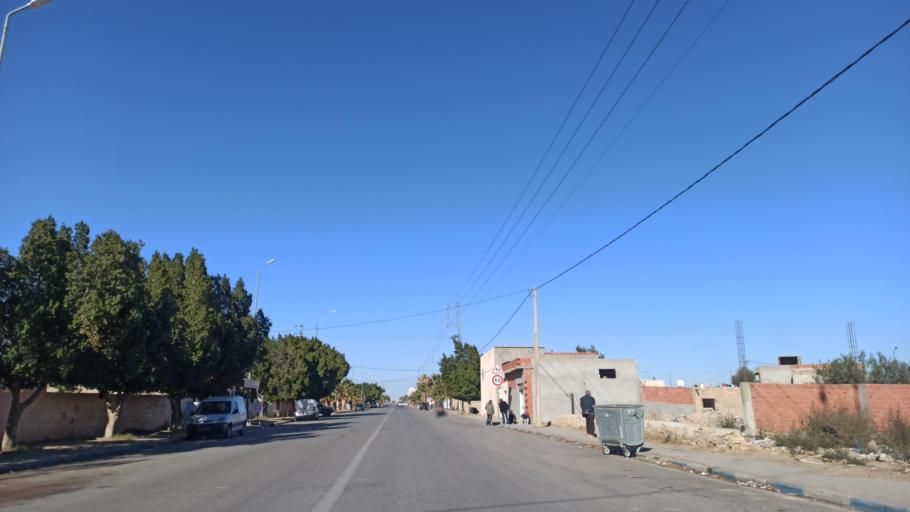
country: TN
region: Sidi Bu Zayd
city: Jilma
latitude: 35.2741
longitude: 9.4190
